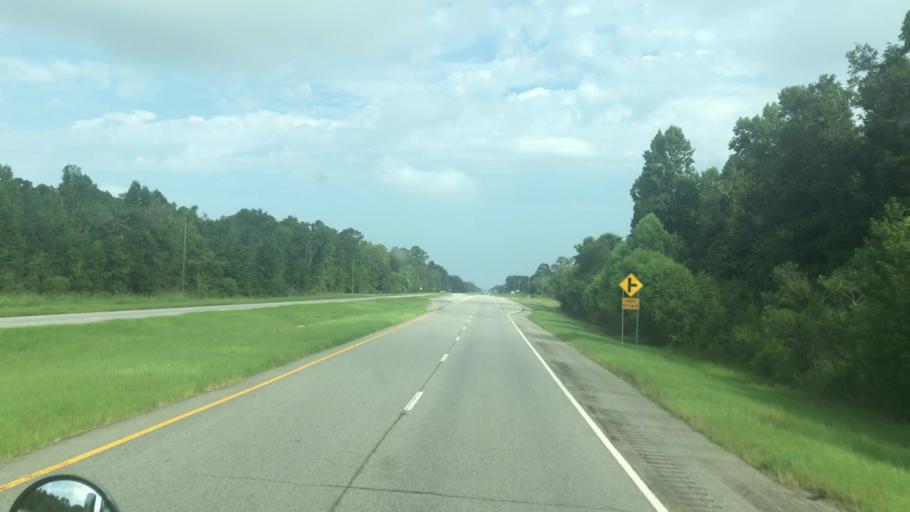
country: US
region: Georgia
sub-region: Miller County
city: Colquitt
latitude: 31.2738
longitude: -84.8298
